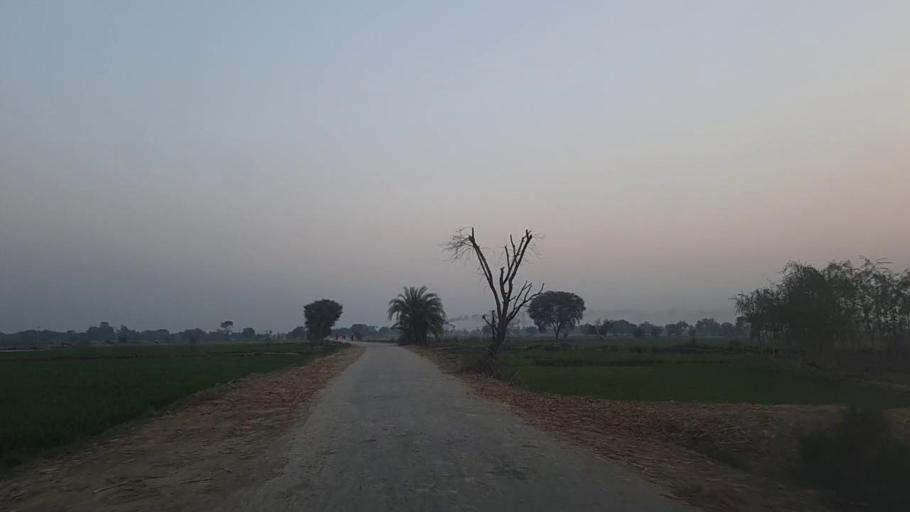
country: PK
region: Sindh
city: Naushahro Firoz
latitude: 26.8609
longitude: 68.0476
